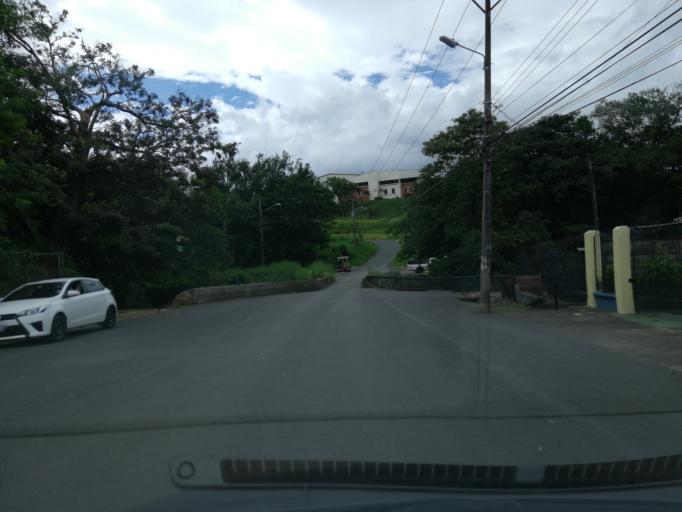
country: CR
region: Alajuela
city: Alajuela
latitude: 9.9994
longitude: -84.2132
